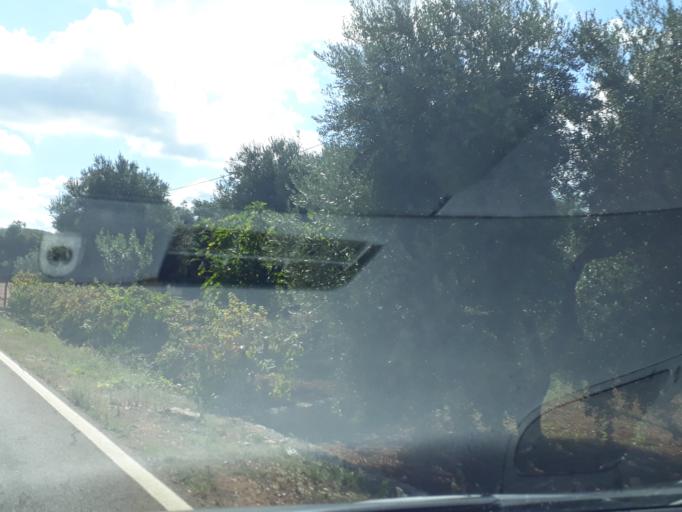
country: IT
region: Apulia
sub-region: Provincia di Brindisi
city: Fasano
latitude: 40.8197
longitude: 17.3770
